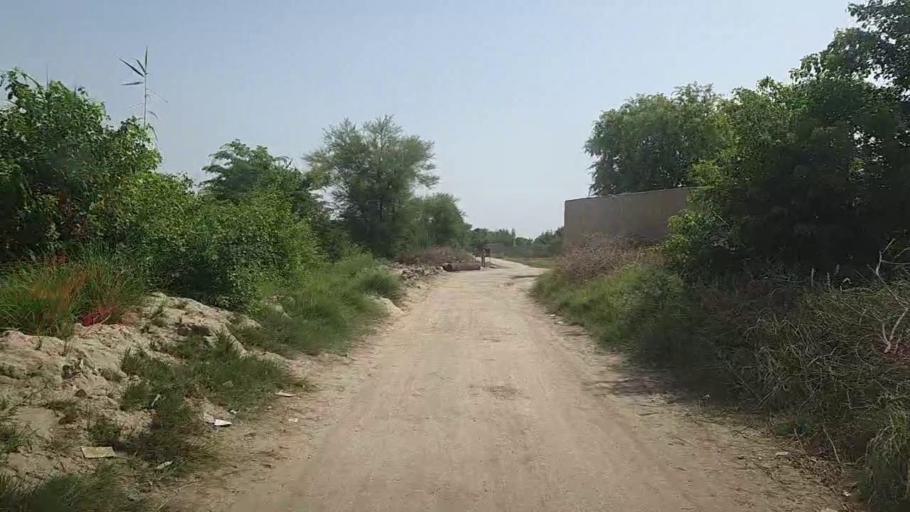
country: PK
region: Sindh
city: Pad Idan
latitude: 26.7955
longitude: 68.3298
